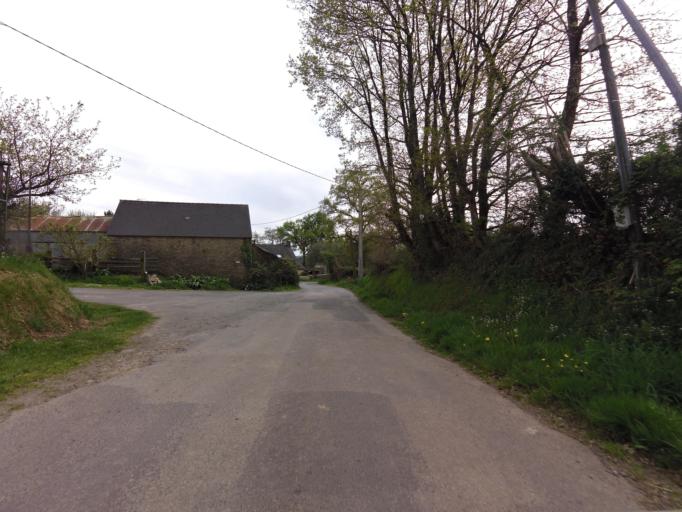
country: FR
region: Brittany
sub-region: Departement du Morbihan
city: Pluherlin
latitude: 47.7201
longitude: -2.3703
